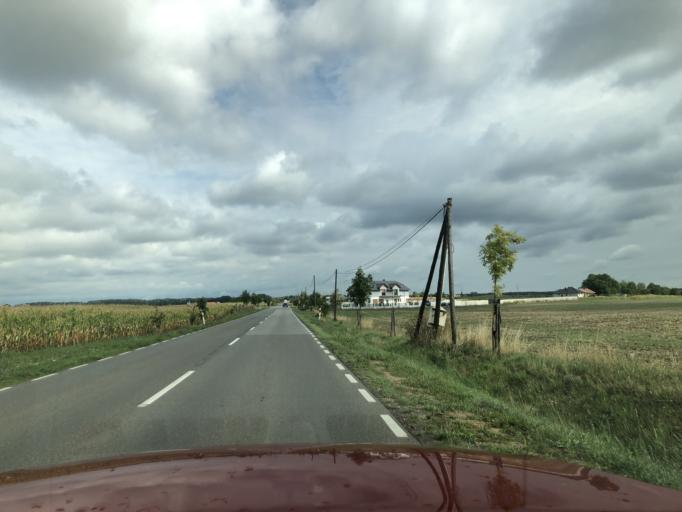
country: PL
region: Greater Poland Voivodeship
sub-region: Powiat szamotulski
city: Pniewy
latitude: 52.5280
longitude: 16.2725
